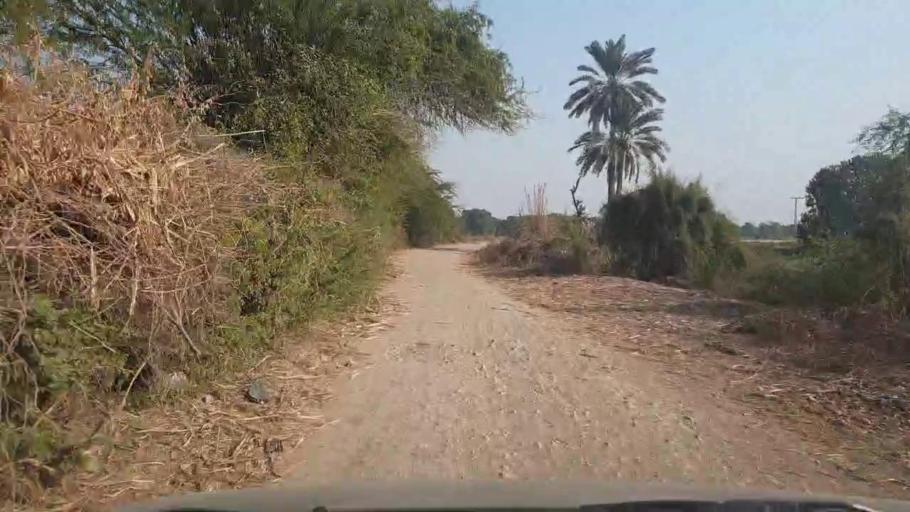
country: PK
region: Sindh
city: Digri
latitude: 25.2460
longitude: 69.1813
